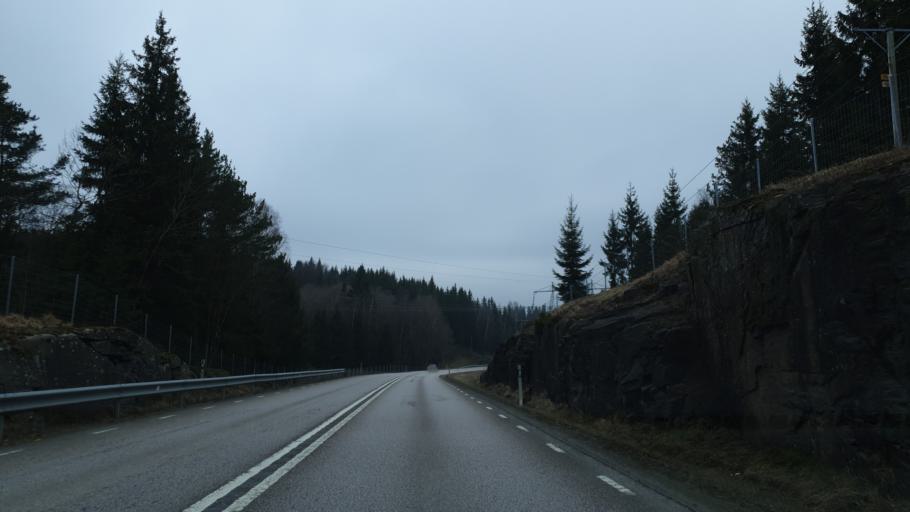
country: SE
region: Vaestra Goetaland
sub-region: Harryda Kommun
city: Hindas
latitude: 57.6387
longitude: 12.4068
